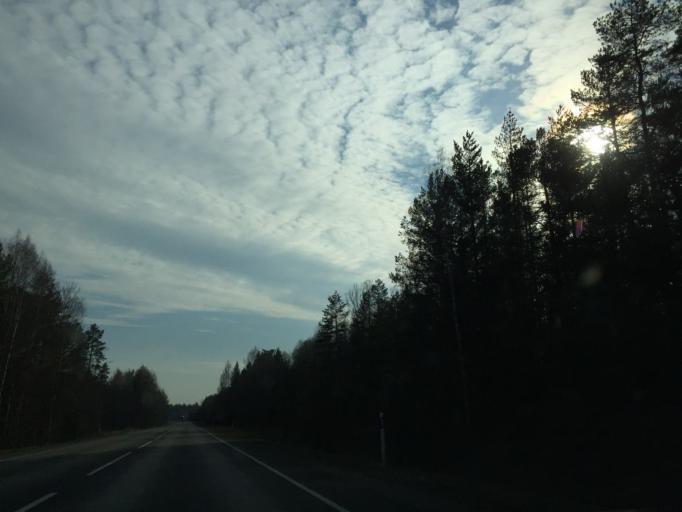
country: EE
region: Ida-Virumaa
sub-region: Kohtla-Nomme vald
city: Kohtla-Nomme
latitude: 59.0297
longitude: 27.2350
